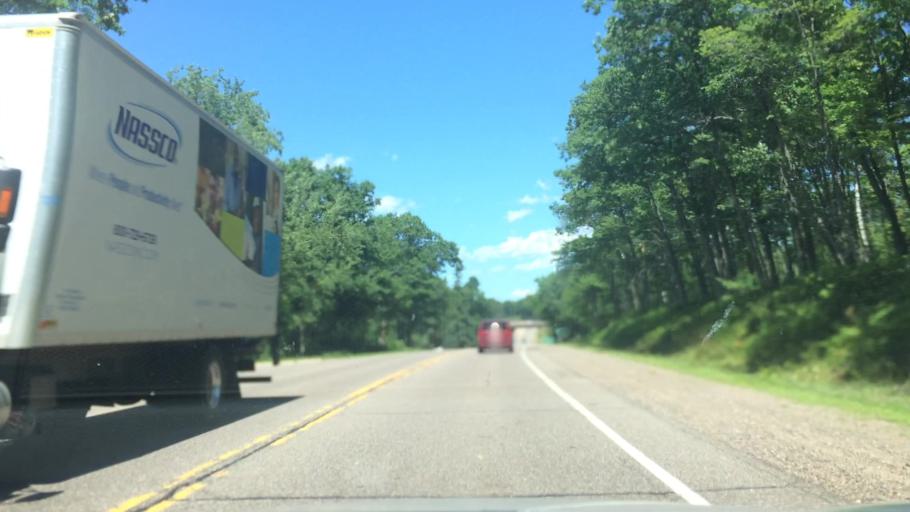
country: US
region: Wisconsin
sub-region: Vilas County
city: Lac du Flambeau
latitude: 45.7805
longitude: -89.7143
